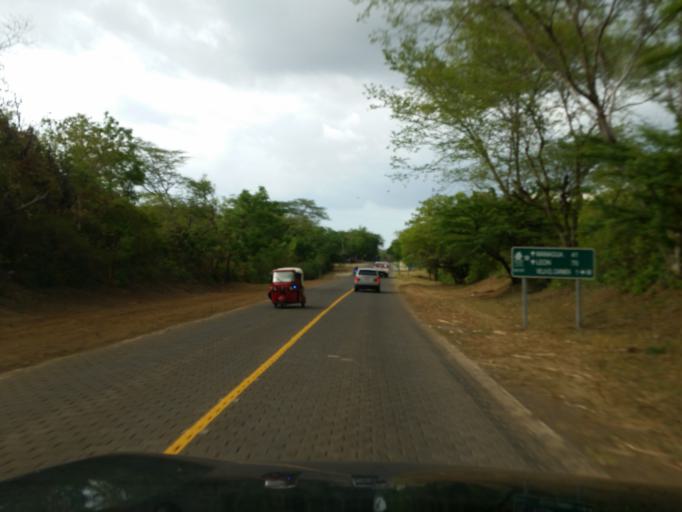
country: NI
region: Managua
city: Carlos Fonseca Amador
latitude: 11.9820
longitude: -86.5154
